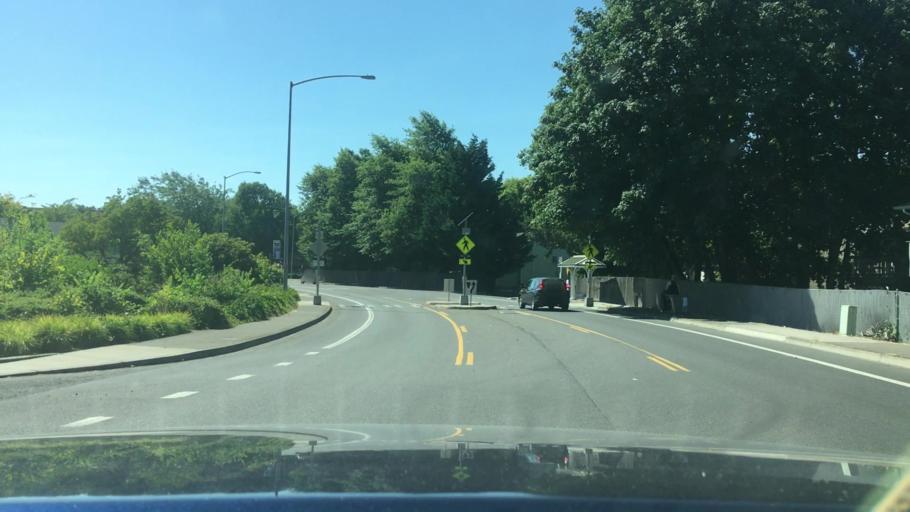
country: US
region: Oregon
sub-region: Lane County
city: Eugene
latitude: 44.0931
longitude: -123.0918
